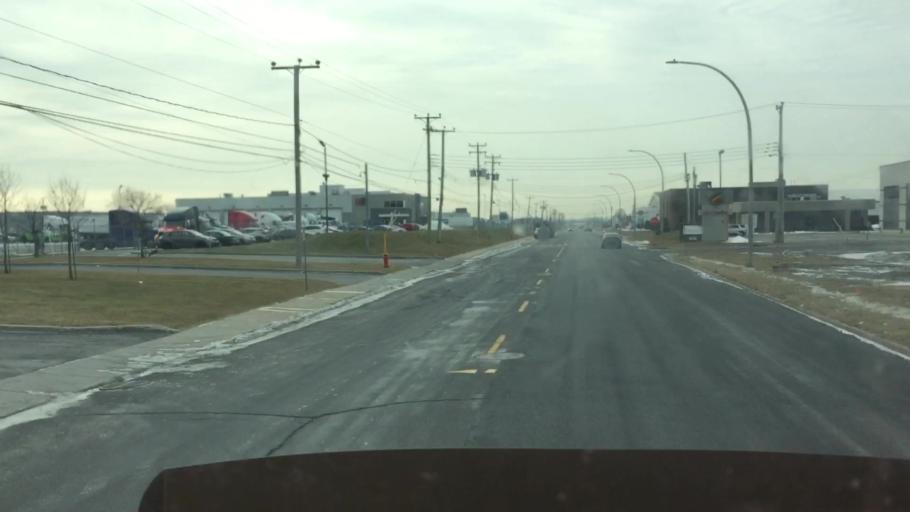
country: CA
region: Quebec
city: Dorval
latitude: 45.4728
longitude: -73.7136
